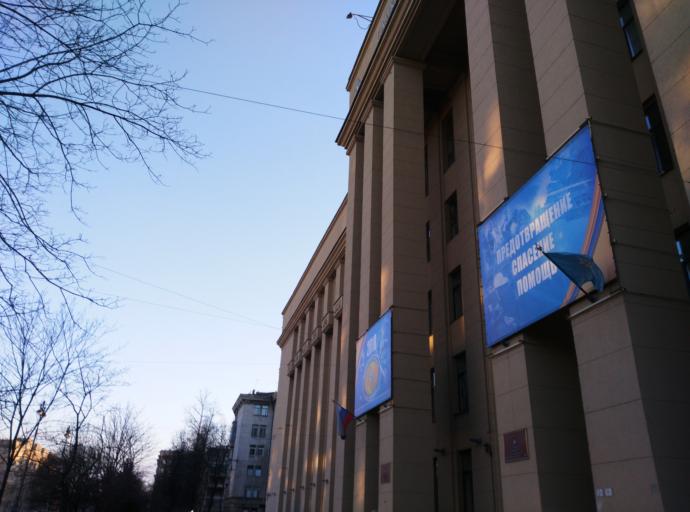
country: RU
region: St.-Petersburg
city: Kupchino
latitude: 59.8752
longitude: 30.3195
